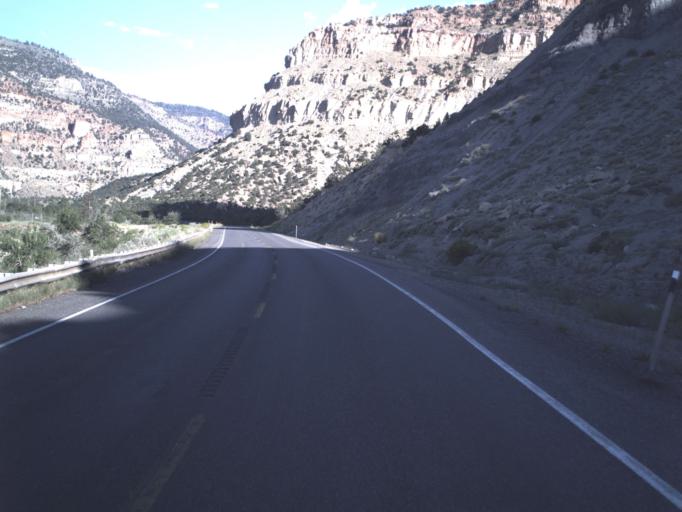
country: US
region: Utah
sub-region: Emery County
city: Huntington
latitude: 39.3906
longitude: -111.0903
